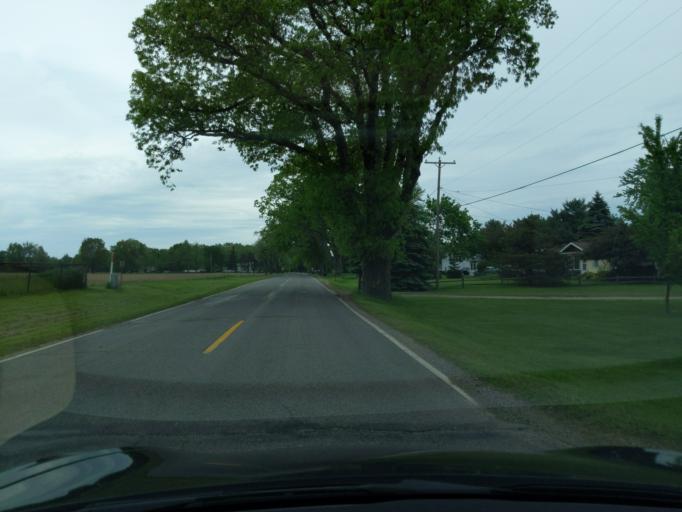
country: US
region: Michigan
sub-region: Ingham County
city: Leslie
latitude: 42.3834
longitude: -84.3493
